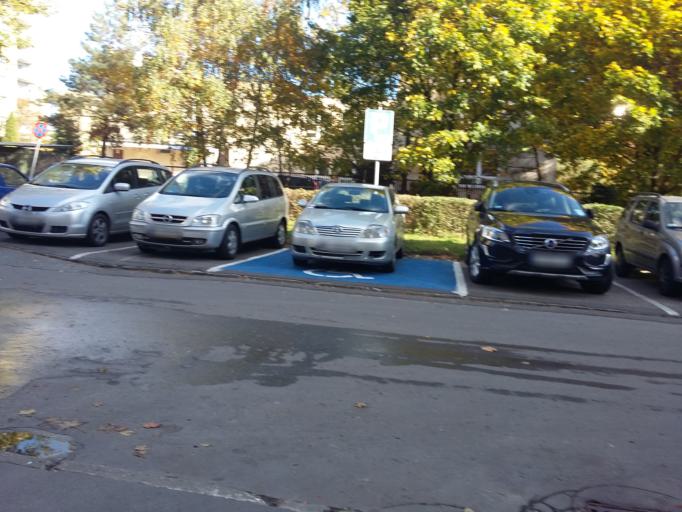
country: PL
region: Lodz Voivodeship
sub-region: Powiat pabianicki
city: Ksawerow
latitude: 51.7448
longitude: 19.4018
